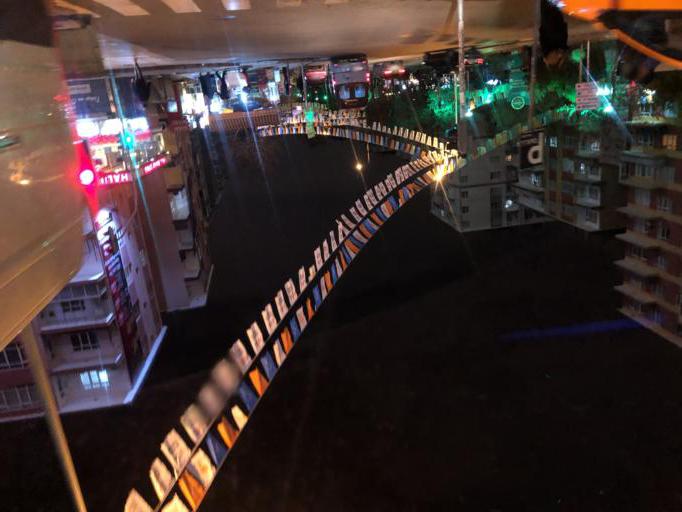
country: TR
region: Ankara
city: Batikent
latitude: 39.9690
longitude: 32.7843
